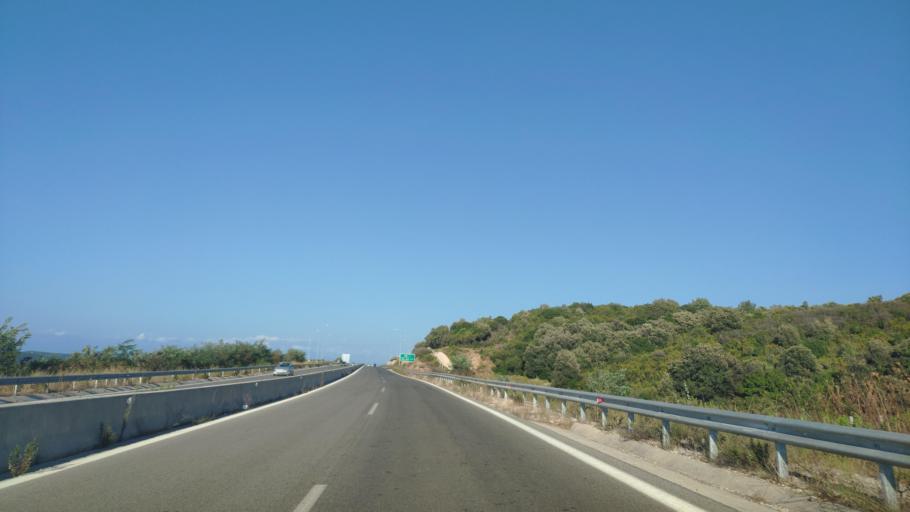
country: GR
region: West Greece
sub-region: Nomos Aitolias kai Akarnanias
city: Vonitsa
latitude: 38.9132
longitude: 20.8118
